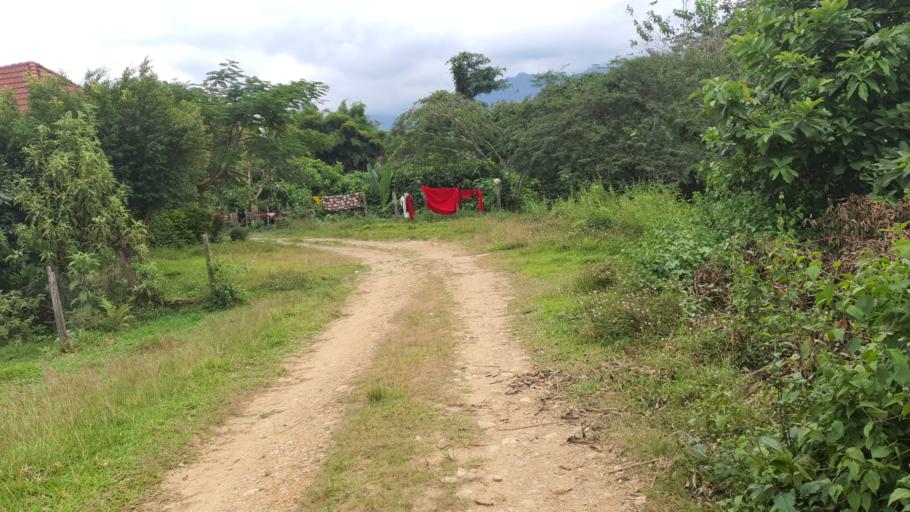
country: LA
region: Bolikhamxai
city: Bolikhan
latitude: 18.9504
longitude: 103.7887
